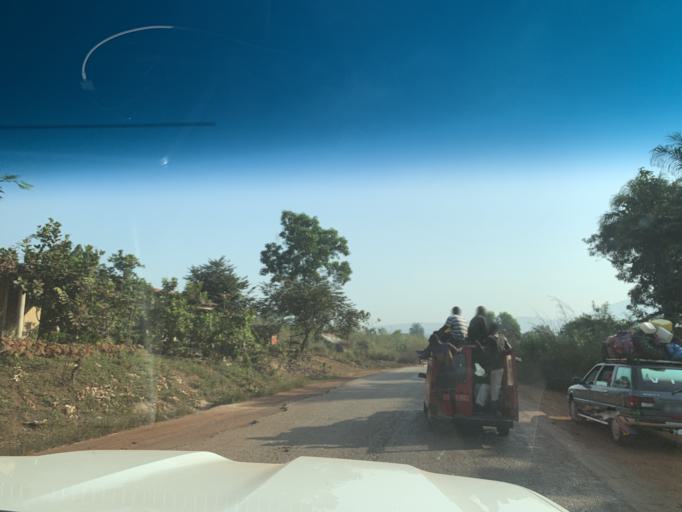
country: GN
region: Kindia
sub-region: Coyah
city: Coyah
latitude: 9.8046
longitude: -13.2827
